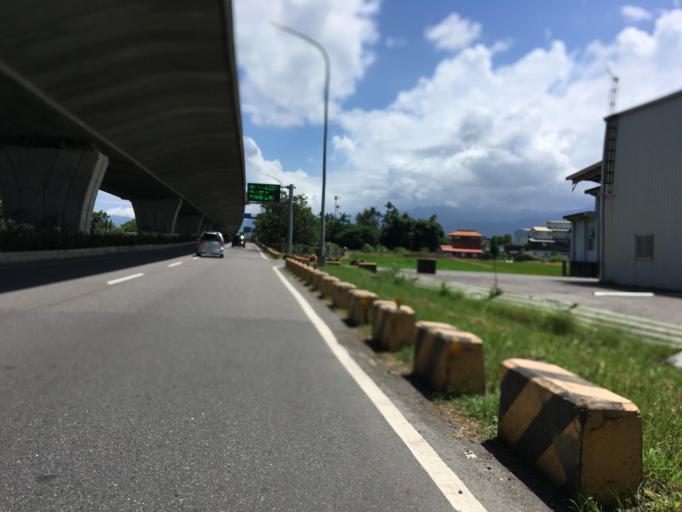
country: TW
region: Taiwan
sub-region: Yilan
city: Yilan
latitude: 24.6864
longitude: 121.7916
